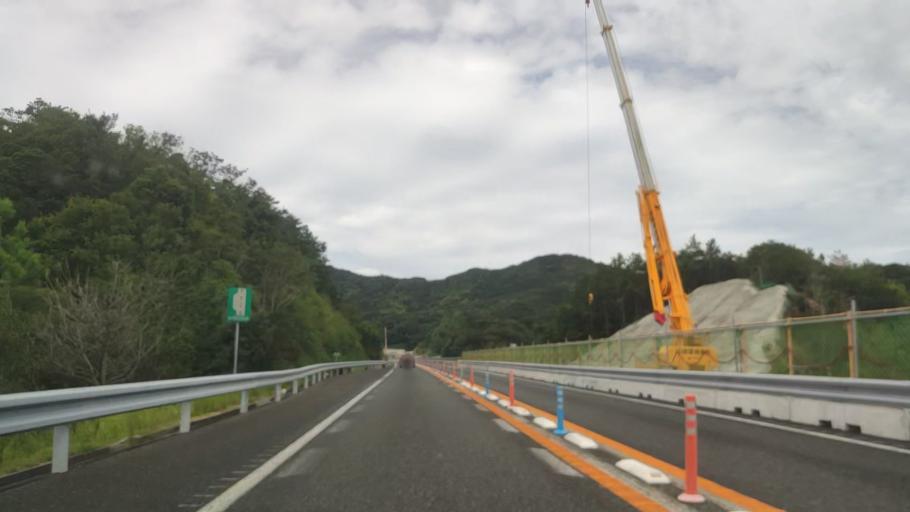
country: JP
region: Wakayama
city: Gobo
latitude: 33.8435
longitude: 135.2191
